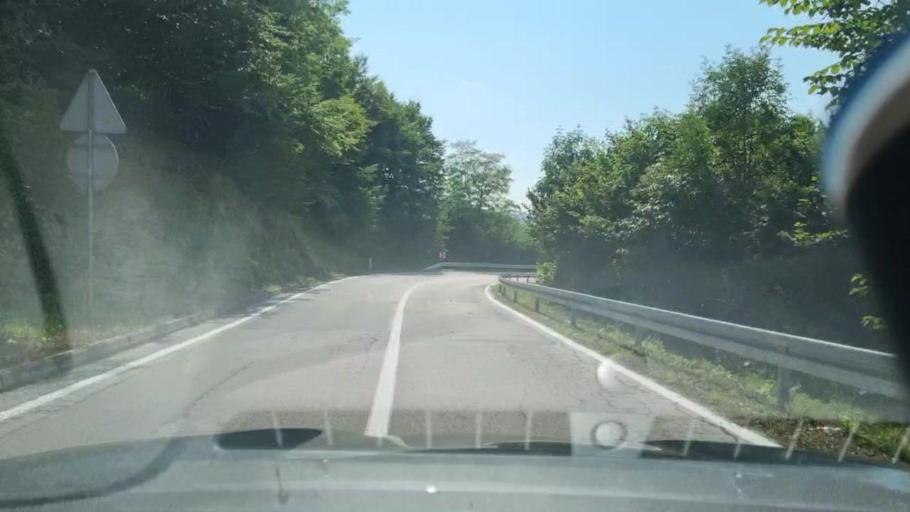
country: BA
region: Federation of Bosnia and Herzegovina
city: Bosanska Krupa
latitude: 44.8399
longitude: 16.1618
